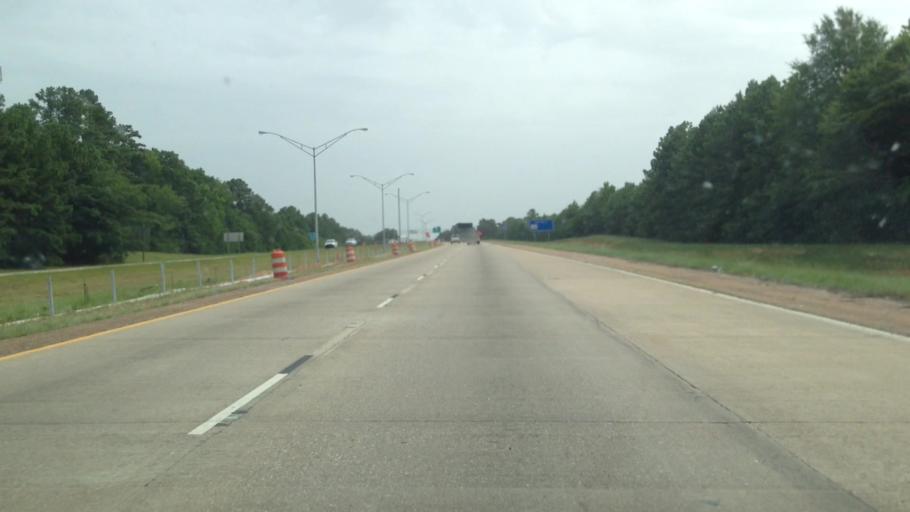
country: US
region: Louisiana
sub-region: Caddo Parish
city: Shreveport
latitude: 32.4898
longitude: -93.8249
